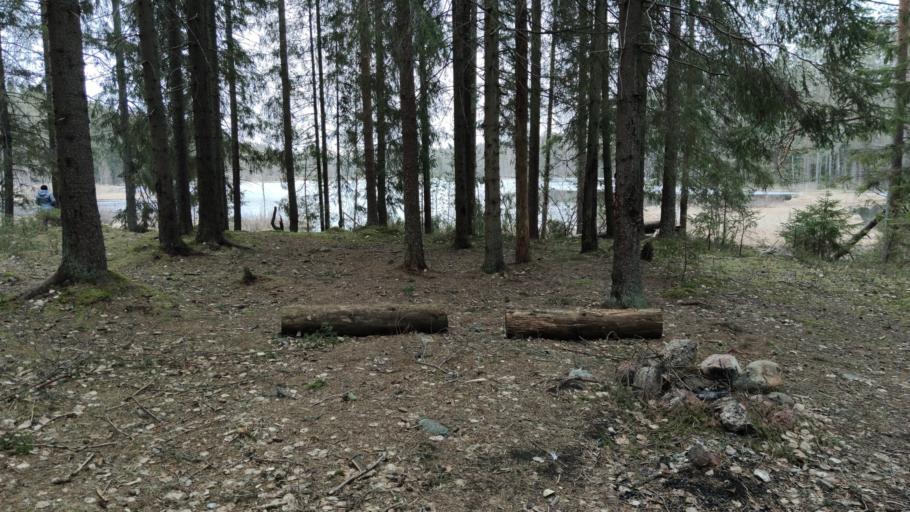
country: RU
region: Leningrad
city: Michurinskoye
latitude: 60.5009
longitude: 29.9952
